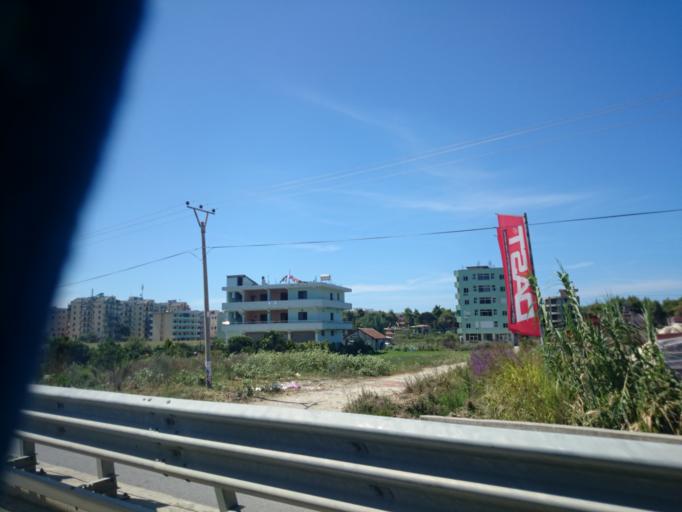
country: AL
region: Tirane
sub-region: Rrethi i Kavajes
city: Golem
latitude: 41.2548
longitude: 19.5263
